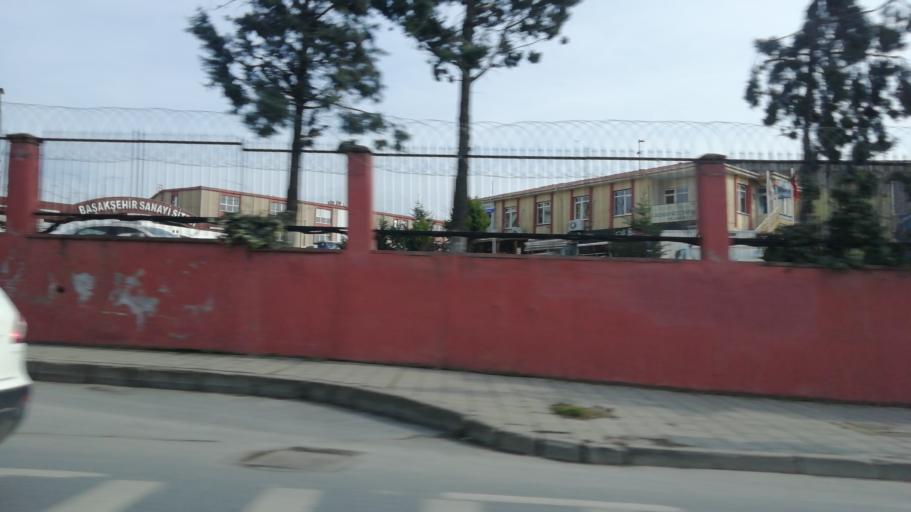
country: TR
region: Istanbul
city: Basaksehir
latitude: 41.1015
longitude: 28.7932
